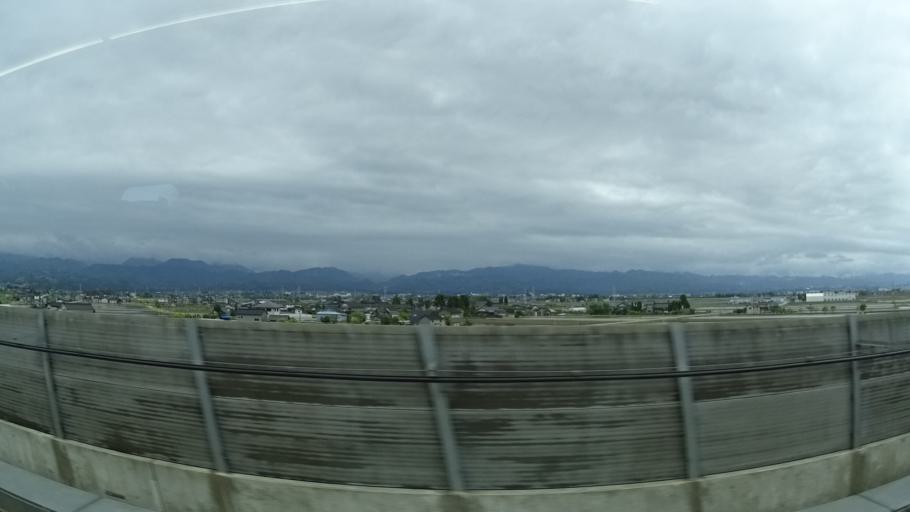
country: JP
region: Toyama
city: Namerikawa
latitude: 36.7305
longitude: 137.3334
